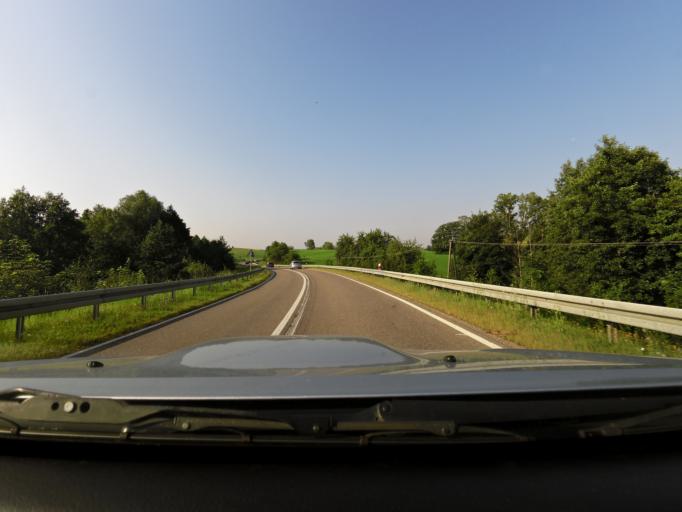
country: PL
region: Podlasie
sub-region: Powiat sejnenski
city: Sejny
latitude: 54.1149
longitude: 23.4243
